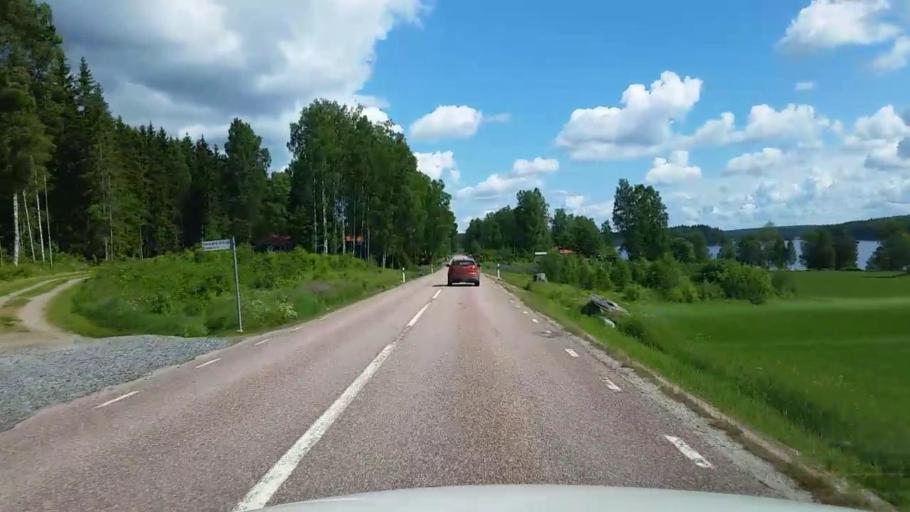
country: SE
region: Vaestmanland
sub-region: Skinnskattebergs Kommun
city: Skinnskatteberg
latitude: 59.7550
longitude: 15.8164
